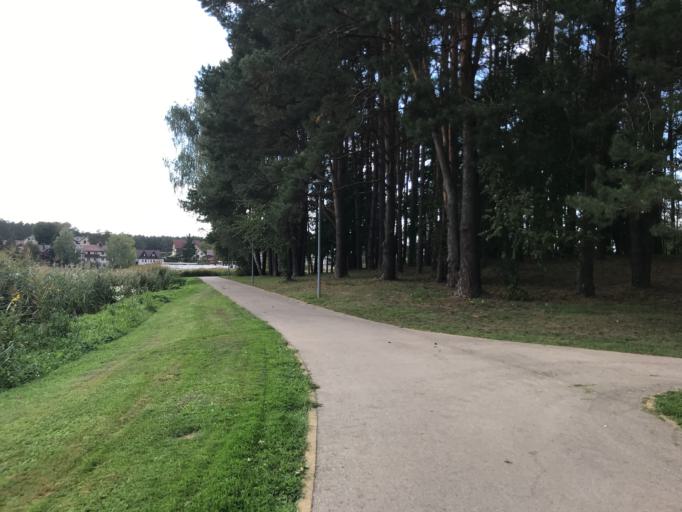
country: LT
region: Alytaus apskritis
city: Druskininkai
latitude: 54.0177
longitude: 23.9641
